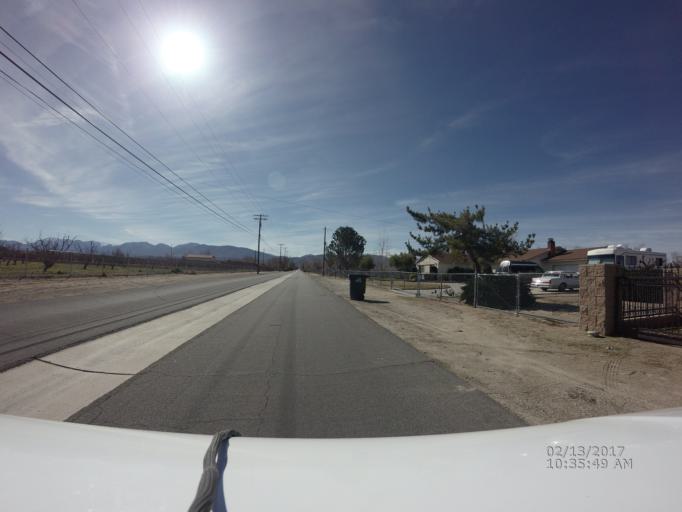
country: US
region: California
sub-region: Los Angeles County
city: Littlerock
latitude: 34.5406
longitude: -117.9793
